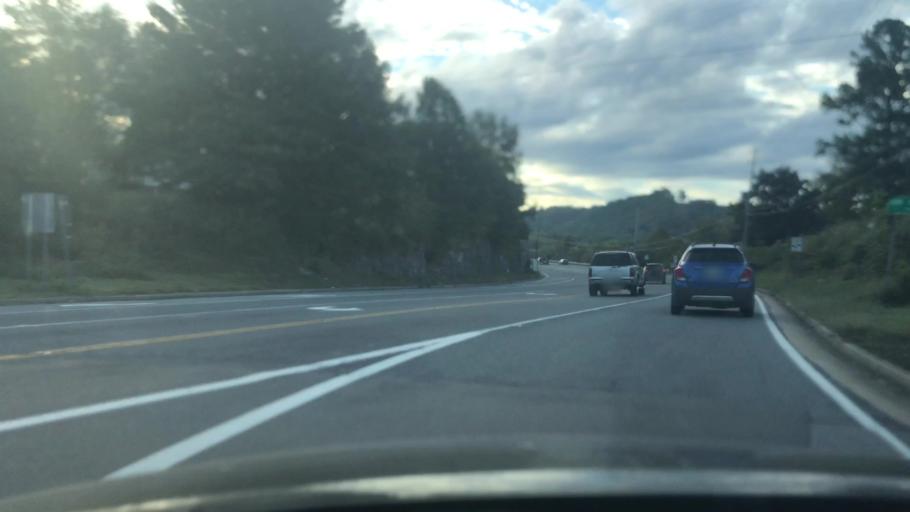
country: US
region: Tennessee
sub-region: Cheatham County
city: Ashland City
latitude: 36.2645
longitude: -87.0589
